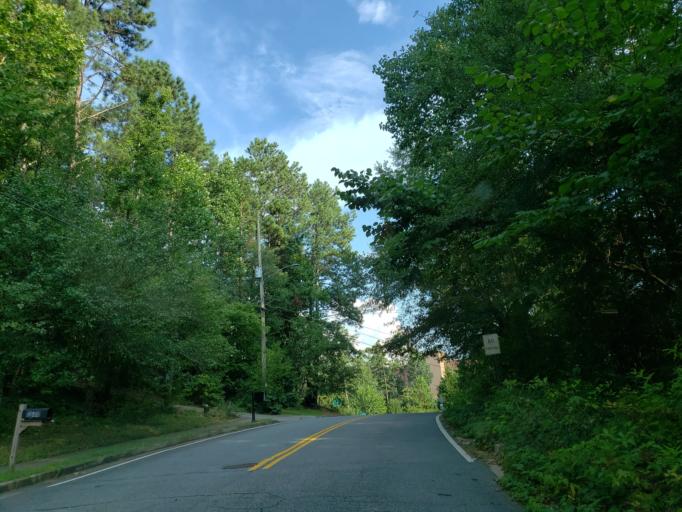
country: US
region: Georgia
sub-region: Cobb County
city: Kennesaw
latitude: 34.0409
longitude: -84.5867
